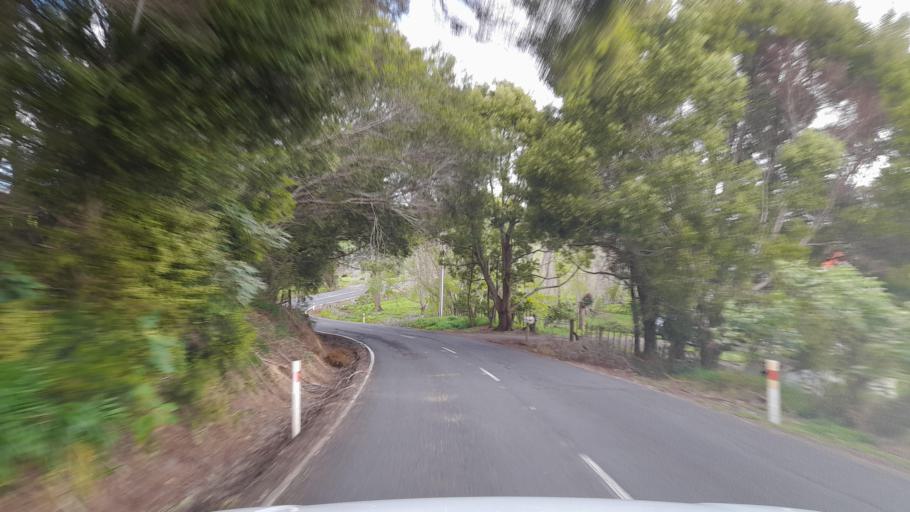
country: NZ
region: Northland
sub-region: Whangarei
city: Maungatapere
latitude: -35.7716
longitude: 174.2452
